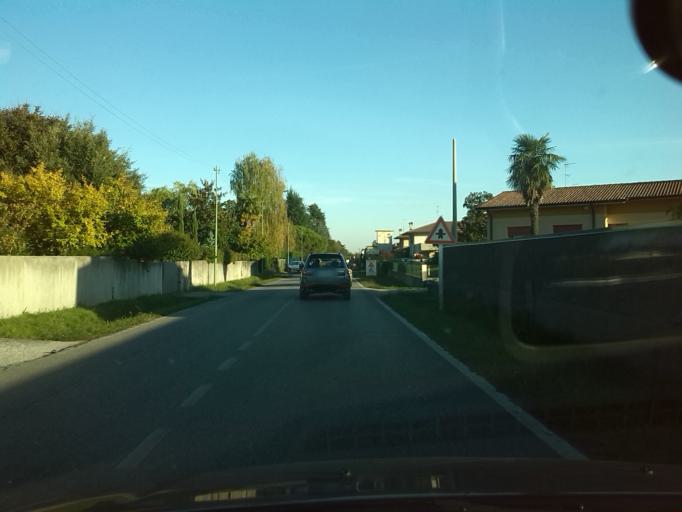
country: IT
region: Friuli Venezia Giulia
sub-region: Provincia di Udine
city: Pagnacco
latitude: 46.0969
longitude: 13.1835
